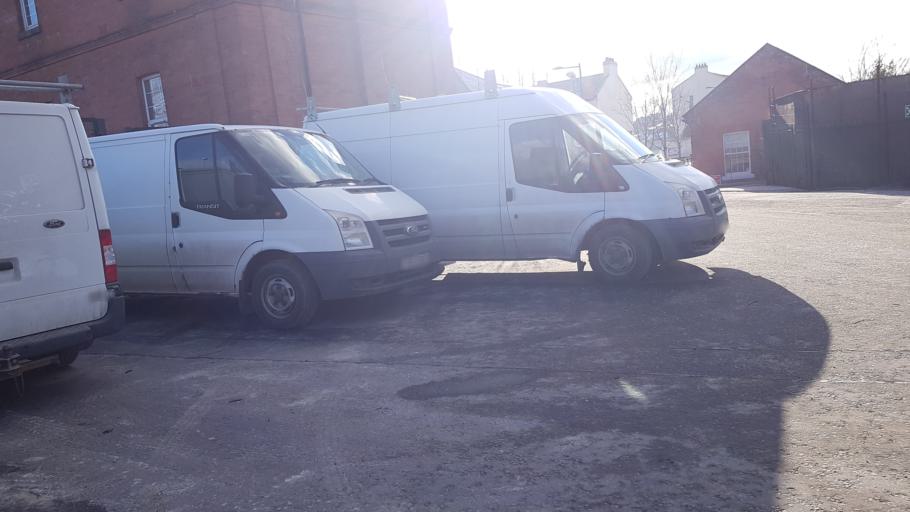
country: GB
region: Northern Ireland
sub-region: City of Derry
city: Derry
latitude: 54.9995
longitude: -7.3102
